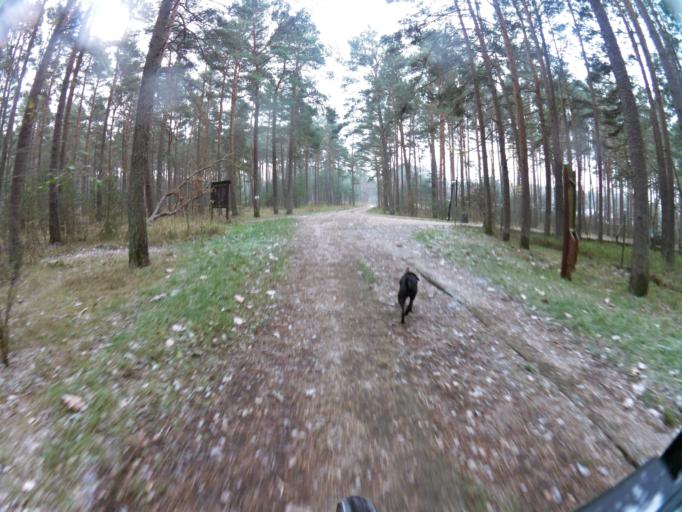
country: PL
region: West Pomeranian Voivodeship
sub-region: Powiat gryficki
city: Cerkwica
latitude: 54.1036
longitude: 15.1313
